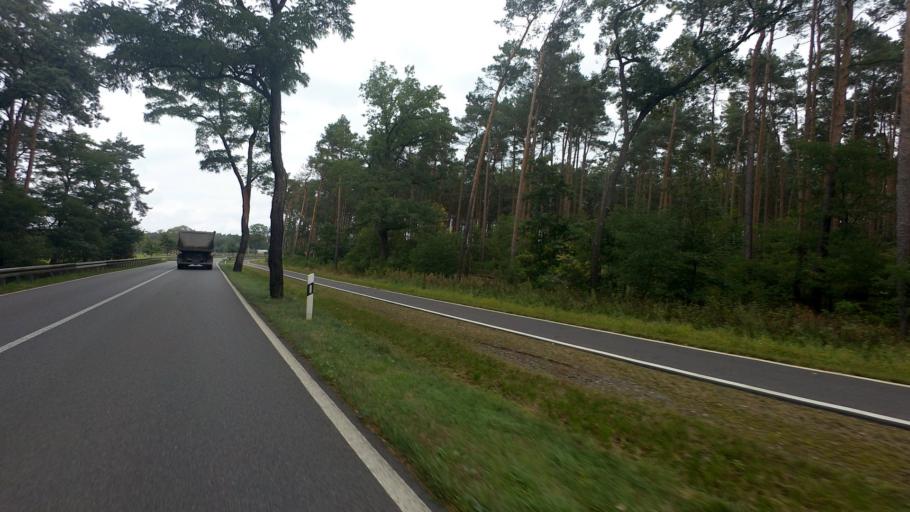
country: DE
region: Brandenburg
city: Schilda
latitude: 51.5694
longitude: 13.3609
